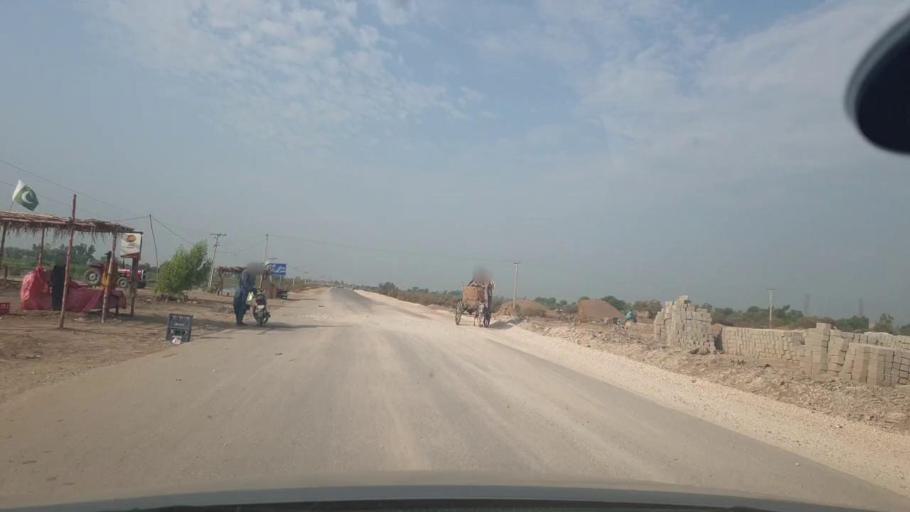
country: PK
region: Sindh
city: Jacobabad
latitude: 28.1374
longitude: 68.3388
